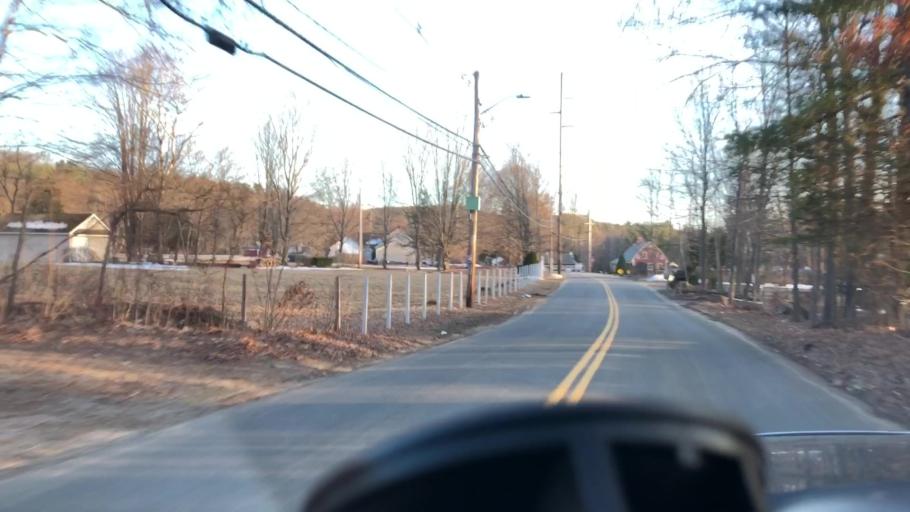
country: US
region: Massachusetts
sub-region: Hampshire County
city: Southampton
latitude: 42.2003
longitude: -72.6797
